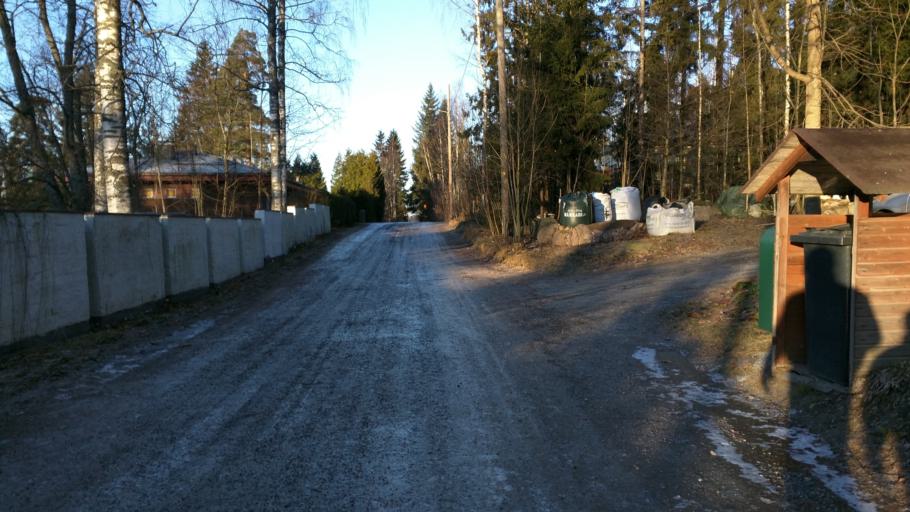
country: FI
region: Uusimaa
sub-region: Helsinki
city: Kilo
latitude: 60.2541
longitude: 24.7629
